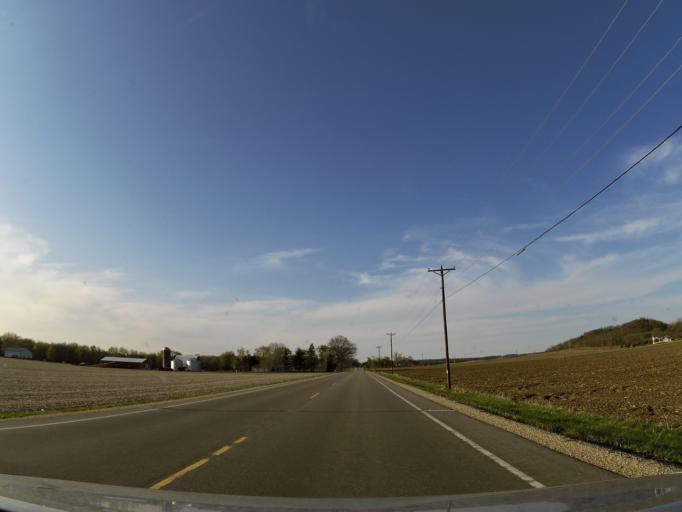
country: US
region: Minnesota
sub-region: Washington County
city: Afton
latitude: 44.8417
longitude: -92.7311
